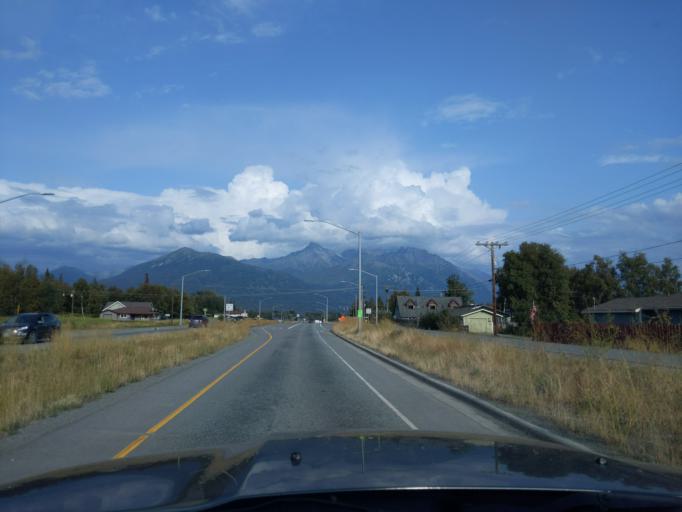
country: US
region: Alaska
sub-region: Matanuska-Susitna Borough
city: Palmer
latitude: 61.6067
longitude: -149.1288
